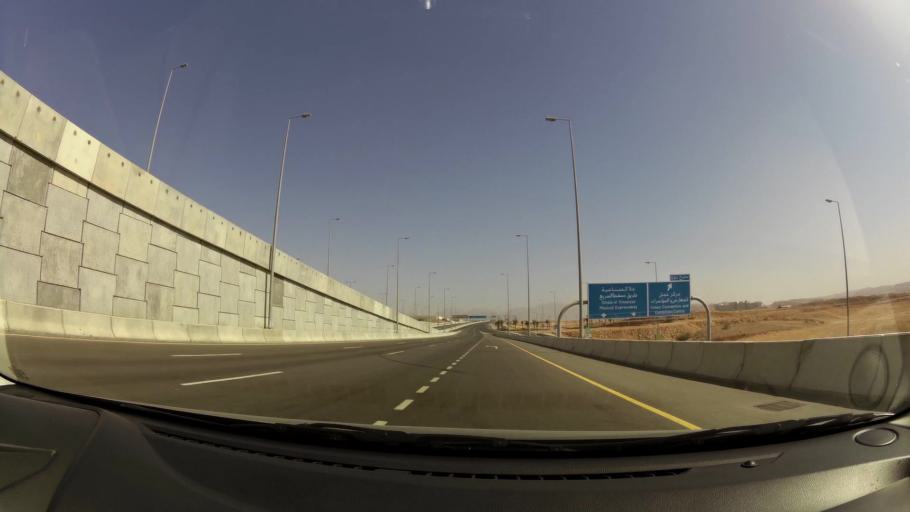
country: OM
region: Muhafazat Masqat
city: Bawshar
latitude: 23.5804
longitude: 58.3326
